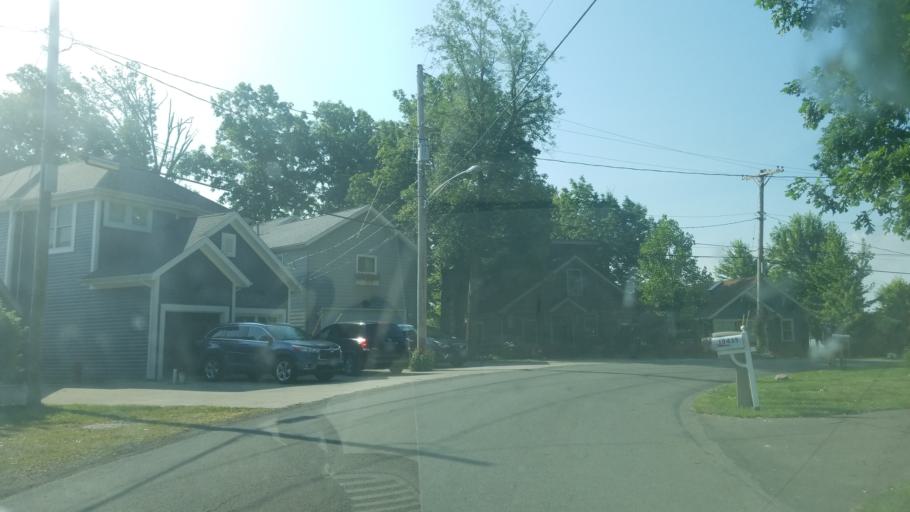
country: US
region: Ohio
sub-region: Logan County
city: Russells Point
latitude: 40.4902
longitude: -83.8746
